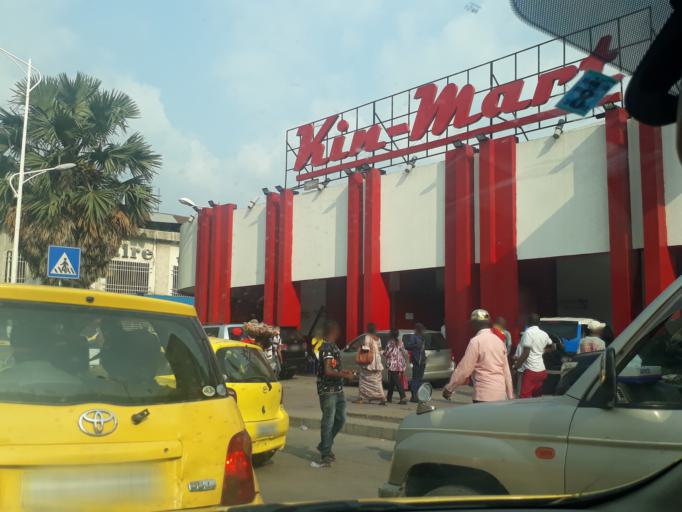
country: CD
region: Kinshasa
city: Kinshasa
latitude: -4.3028
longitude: 15.3123
